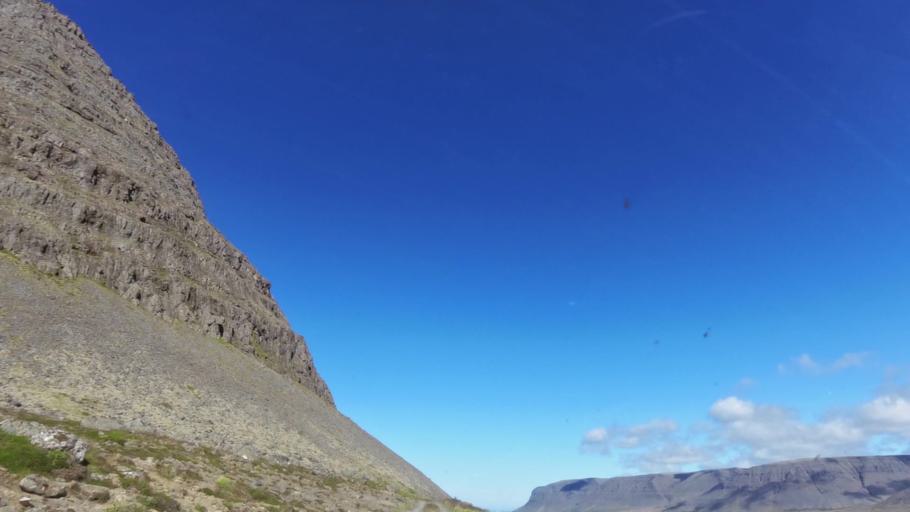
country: IS
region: West
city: Olafsvik
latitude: 65.6262
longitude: -23.8996
